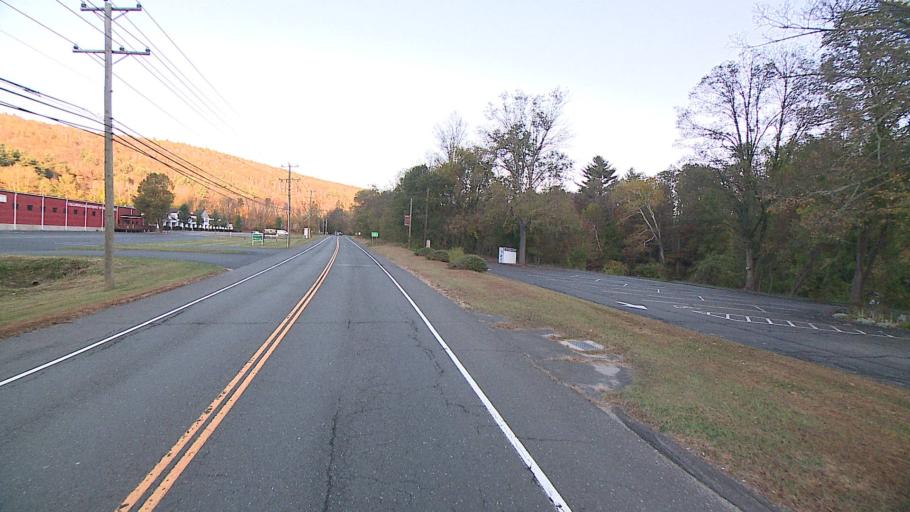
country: US
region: Connecticut
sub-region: Litchfield County
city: New Hartford Center
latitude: 41.8687
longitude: -72.9602
